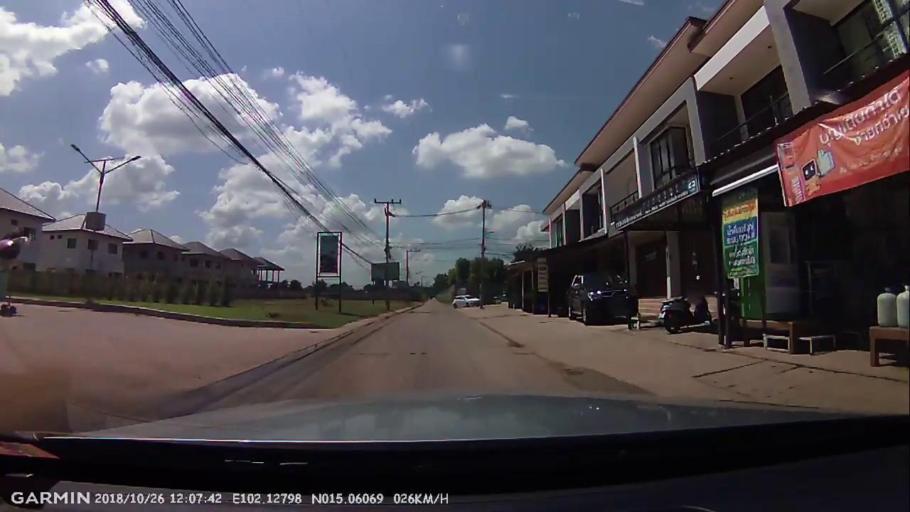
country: TH
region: Nakhon Ratchasima
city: Nakhon Ratchasima
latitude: 15.0607
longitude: 102.1279
